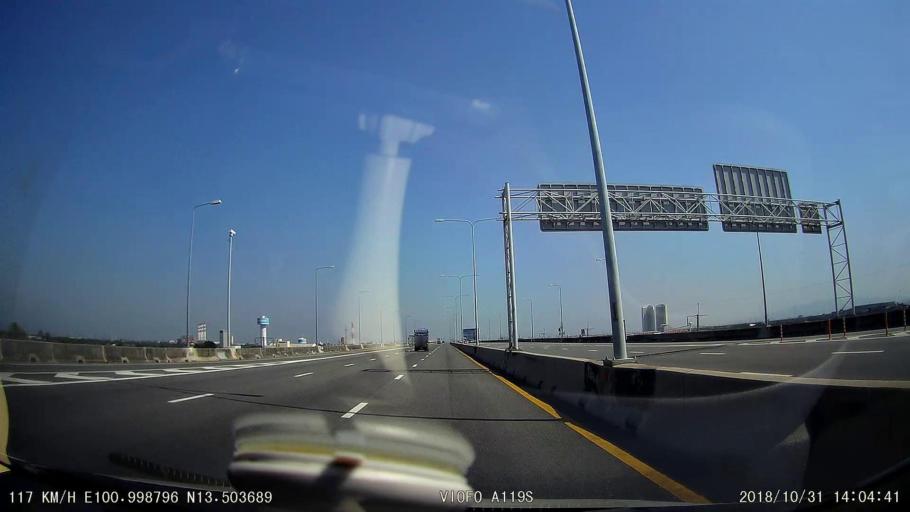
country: TH
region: Chachoengsao
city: Bang Pakong
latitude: 13.5035
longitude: 100.9990
